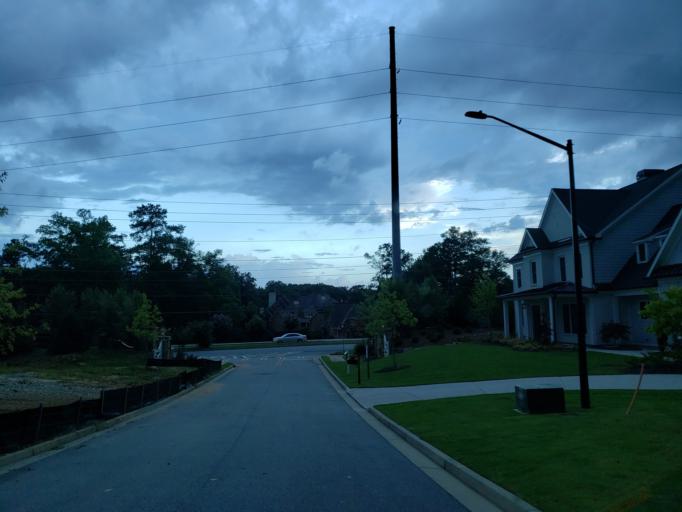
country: US
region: Georgia
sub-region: Fulton County
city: Roswell
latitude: 34.0022
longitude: -84.4000
